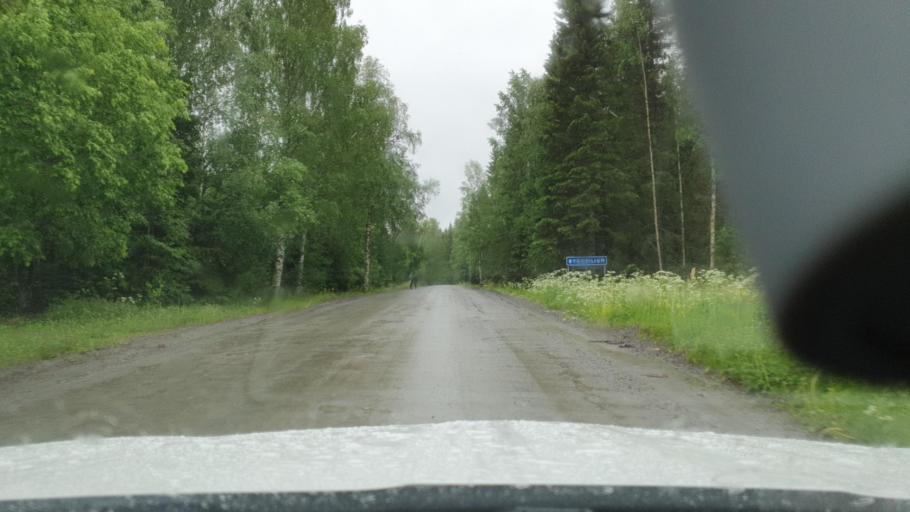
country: SE
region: Vaesterbotten
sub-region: Skelleftea Kommun
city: Burtraesk
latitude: 64.3510
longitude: 20.4831
